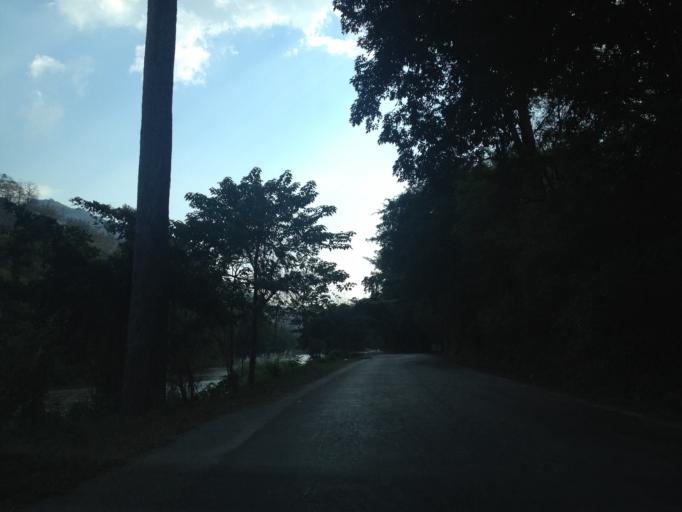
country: TH
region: Chiang Mai
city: Hot
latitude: 18.2349
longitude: 98.5367
